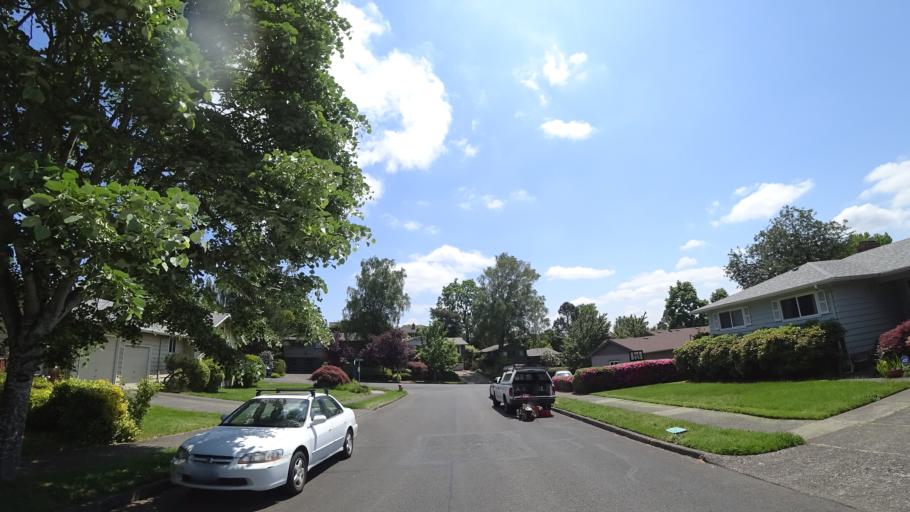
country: US
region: Oregon
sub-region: Multnomah County
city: Portland
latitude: 45.4748
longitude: -122.6919
